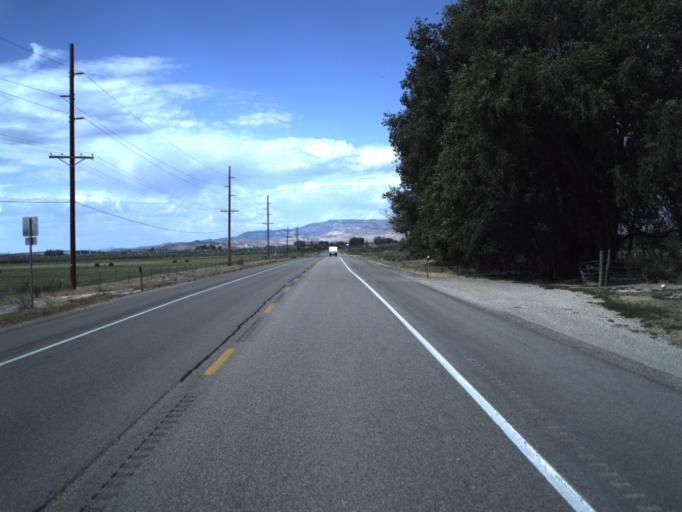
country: US
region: Utah
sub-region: Sanpete County
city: Centerfield
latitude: 39.0699
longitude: -111.8208
